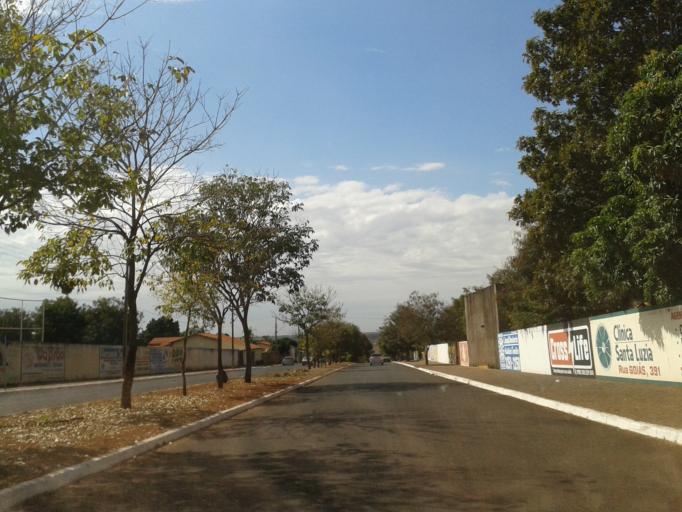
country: BR
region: Minas Gerais
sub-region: Santa Vitoria
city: Santa Vitoria
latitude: -18.8450
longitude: -50.1212
